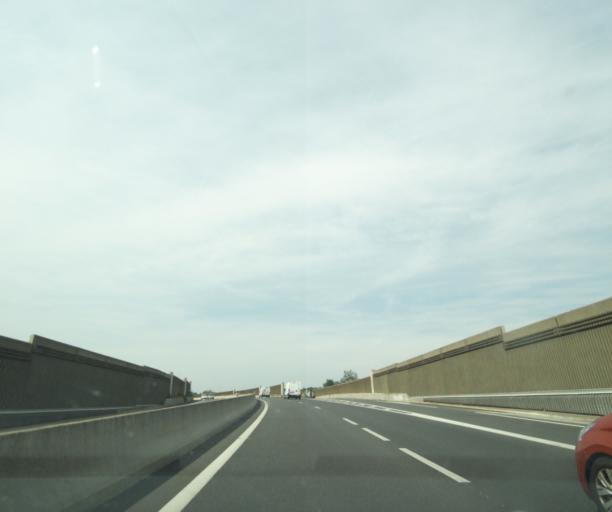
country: FR
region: Centre
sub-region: Departement d'Indre-et-Loire
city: Saint-Cyr-sur-Loire
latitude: 47.3975
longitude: 0.6478
